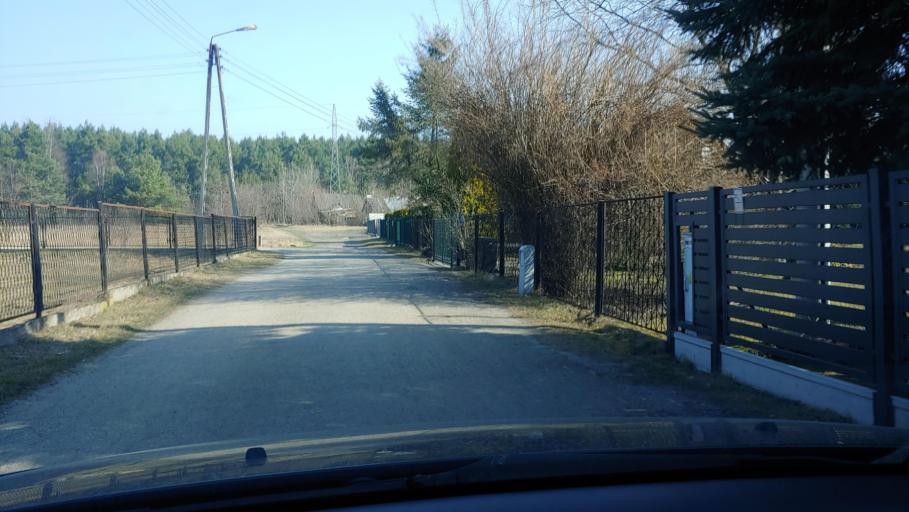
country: PL
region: Lesser Poland Voivodeship
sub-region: Powiat chrzanowski
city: Luszowice
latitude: 50.1546
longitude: 19.4316
